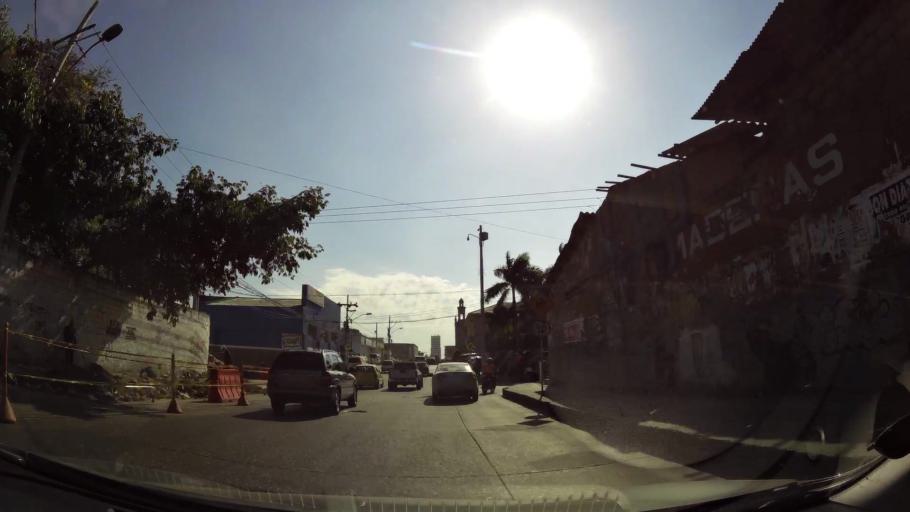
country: CO
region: Atlantico
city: Barranquilla
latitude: 10.9852
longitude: -74.7882
